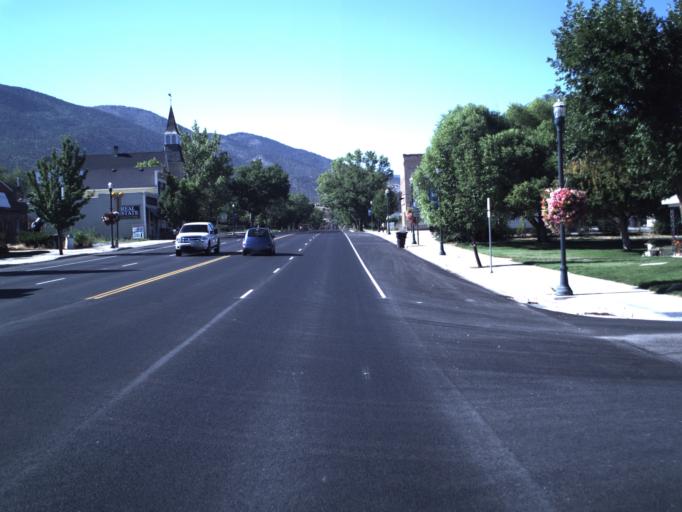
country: US
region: Utah
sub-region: Sanpete County
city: Manti
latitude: 39.2641
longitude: -111.6371
